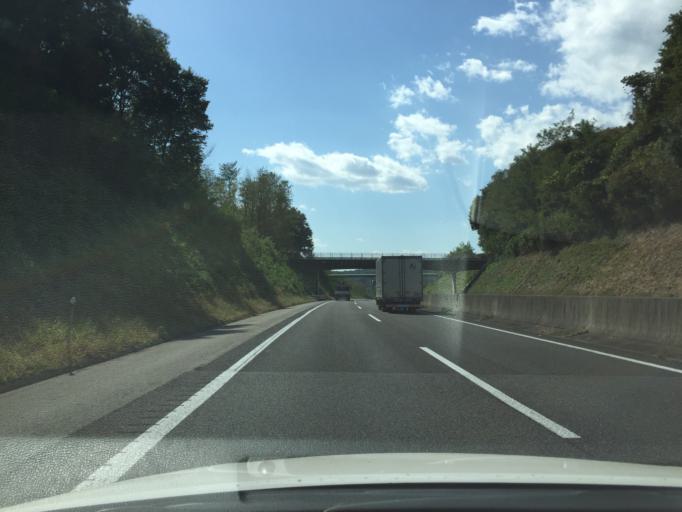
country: JP
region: Fukushima
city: Sukagawa
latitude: 37.2296
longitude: 140.3242
